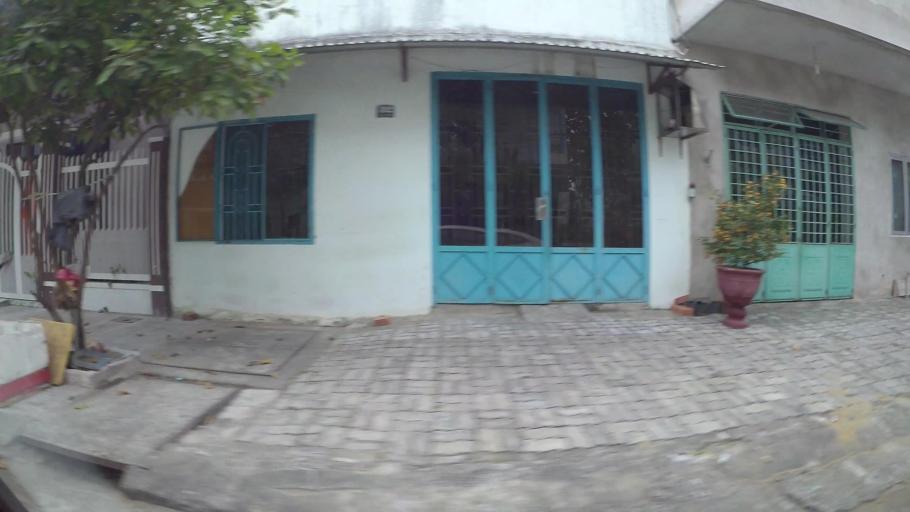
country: VN
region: Da Nang
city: Cam Le
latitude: 16.0268
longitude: 108.2224
